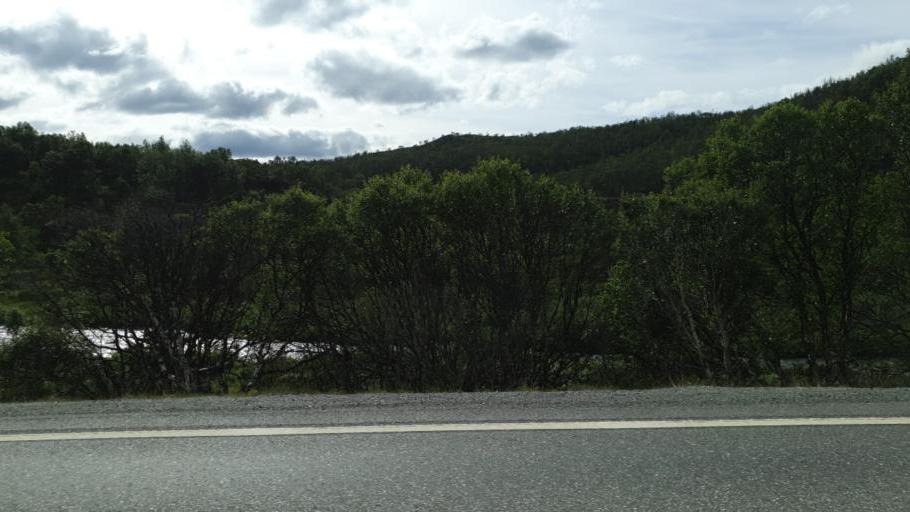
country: NO
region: Sor-Trondelag
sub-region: Oppdal
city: Oppdal
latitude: 62.2922
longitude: 9.5949
